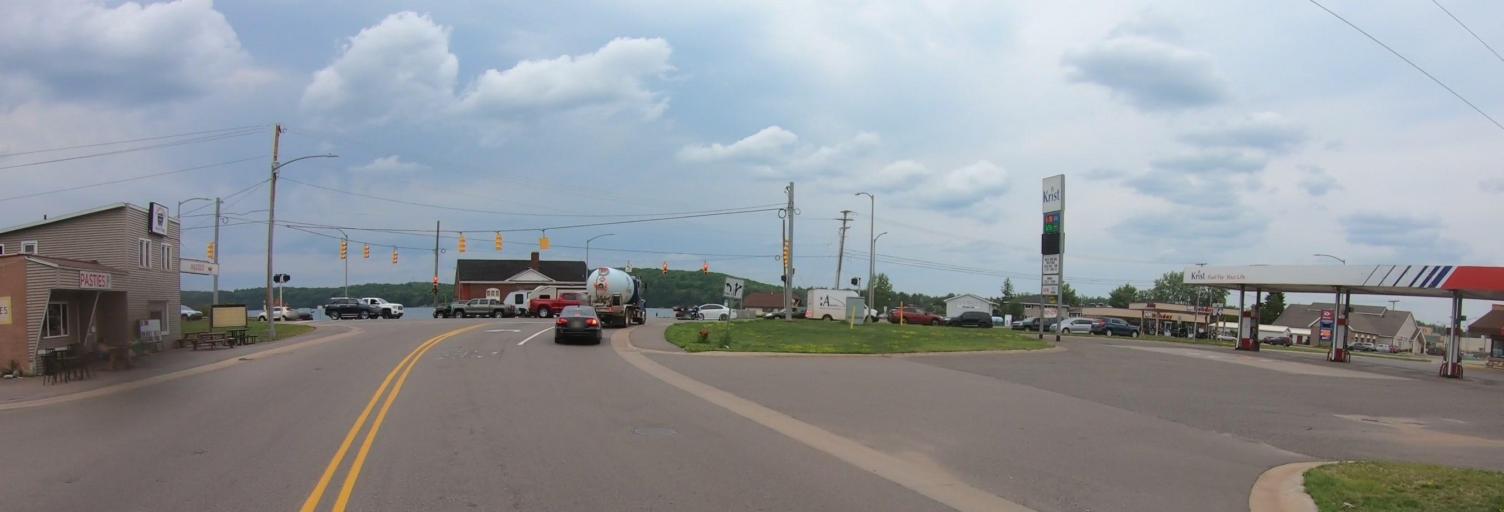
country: US
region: Michigan
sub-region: Marquette County
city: Negaunee
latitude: 46.5077
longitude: -87.6106
